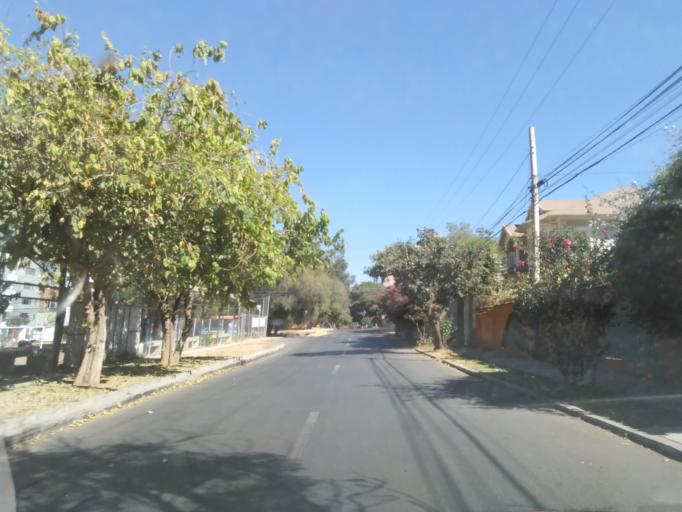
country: BO
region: Cochabamba
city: Cochabamba
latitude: -17.3708
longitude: -66.1487
